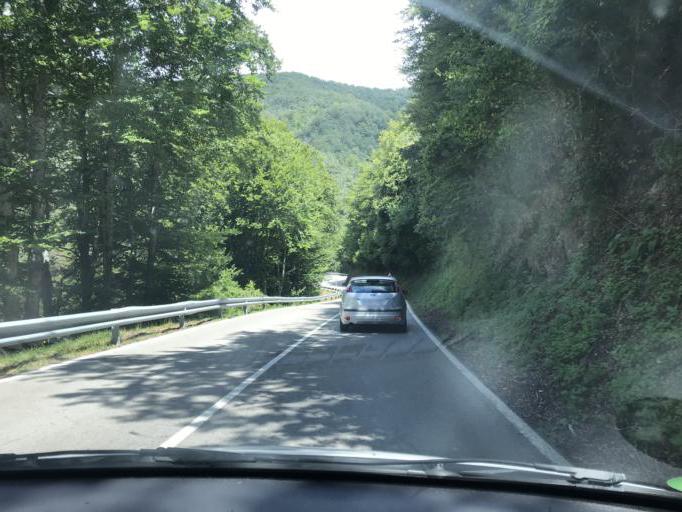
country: ES
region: Cantabria
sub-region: Provincia de Cantabria
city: Cabezon de Liebana
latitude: 43.0760
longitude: -4.4750
